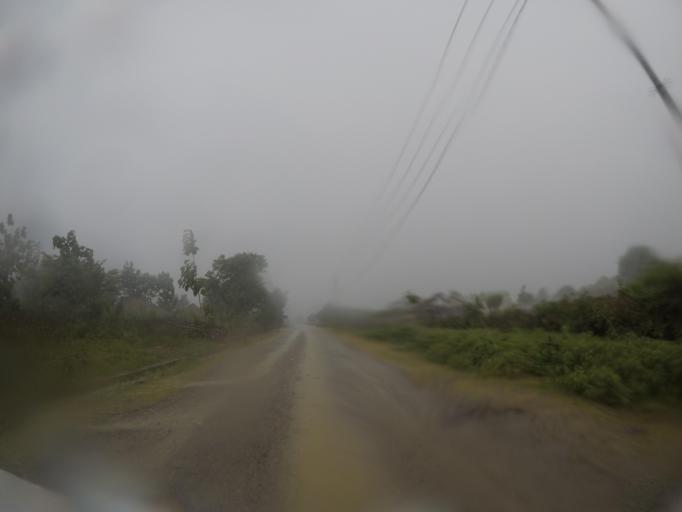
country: TL
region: Bobonaro
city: Maliana
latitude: -8.8575
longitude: 125.1007
